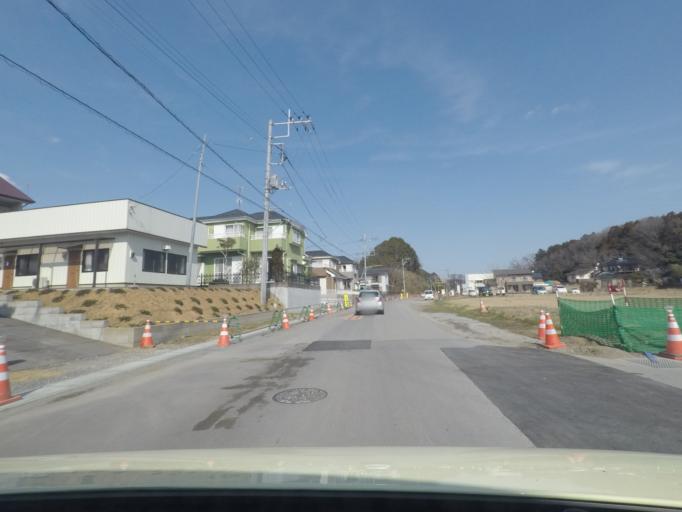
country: JP
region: Ibaraki
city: Ishioka
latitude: 36.1740
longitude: 140.3619
